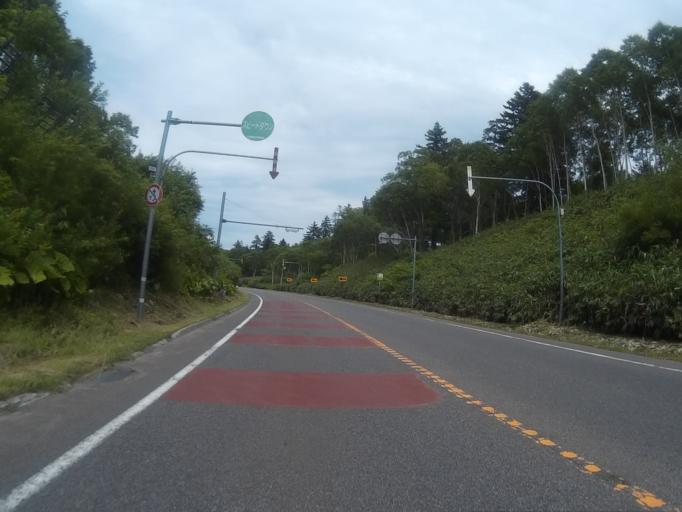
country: JP
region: Hokkaido
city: Sapporo
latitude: 42.8641
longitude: 141.1070
